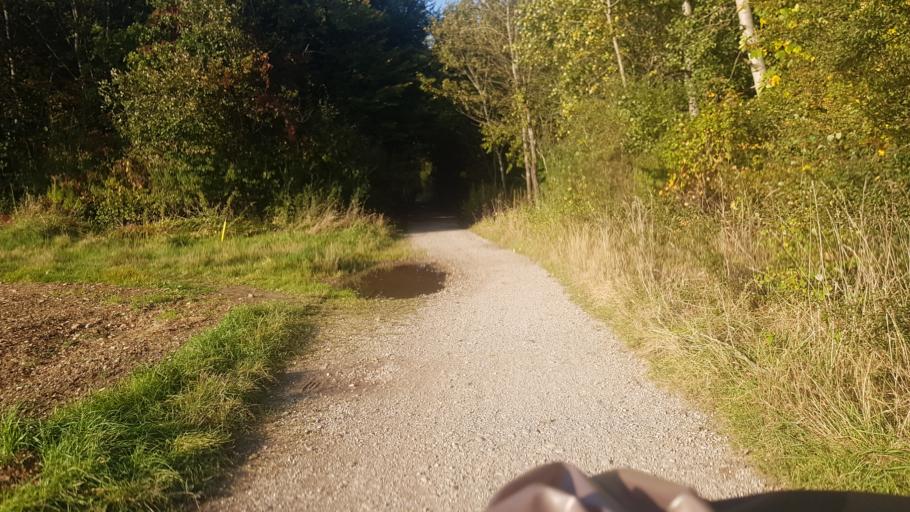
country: DE
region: Bavaria
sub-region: Upper Bavaria
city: Neubiberg
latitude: 48.0980
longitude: 11.6655
